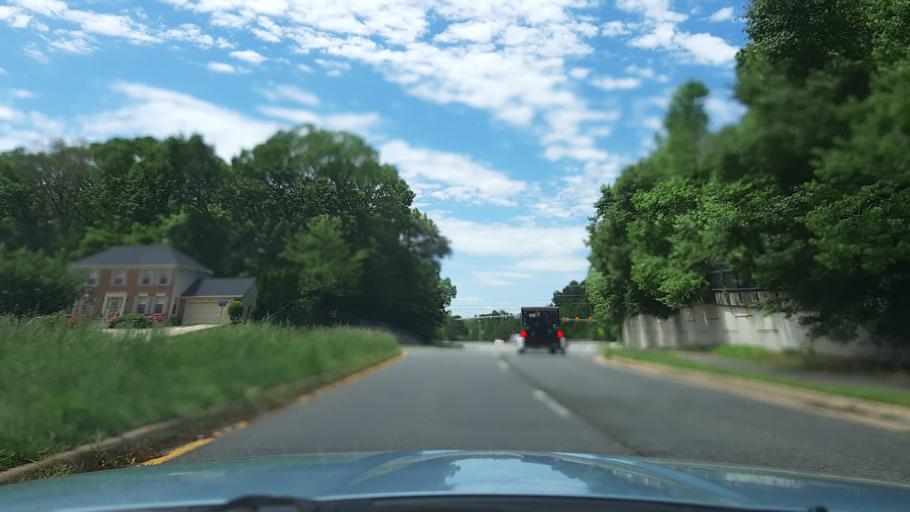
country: US
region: Virginia
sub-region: Fairfax County
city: Burke
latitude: 38.7569
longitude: -77.2757
